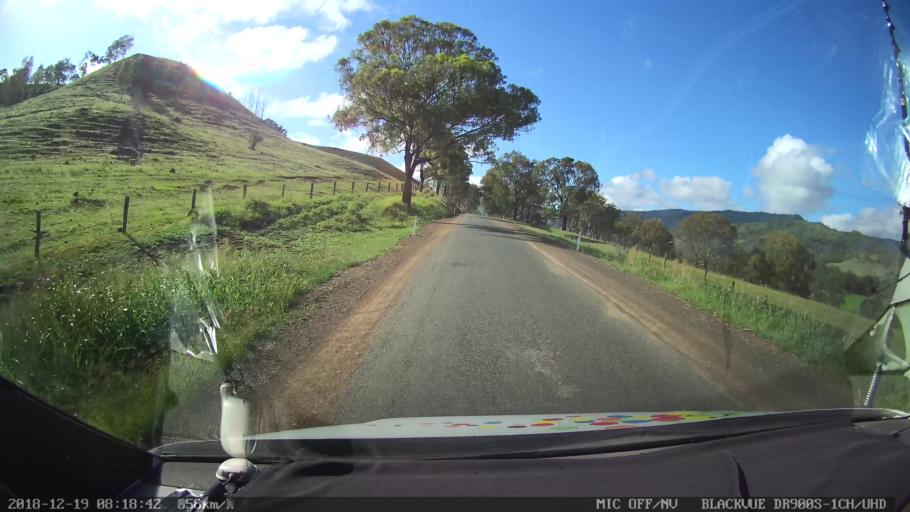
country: AU
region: New South Wales
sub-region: Kyogle
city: Kyogle
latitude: -28.2758
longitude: 152.9090
